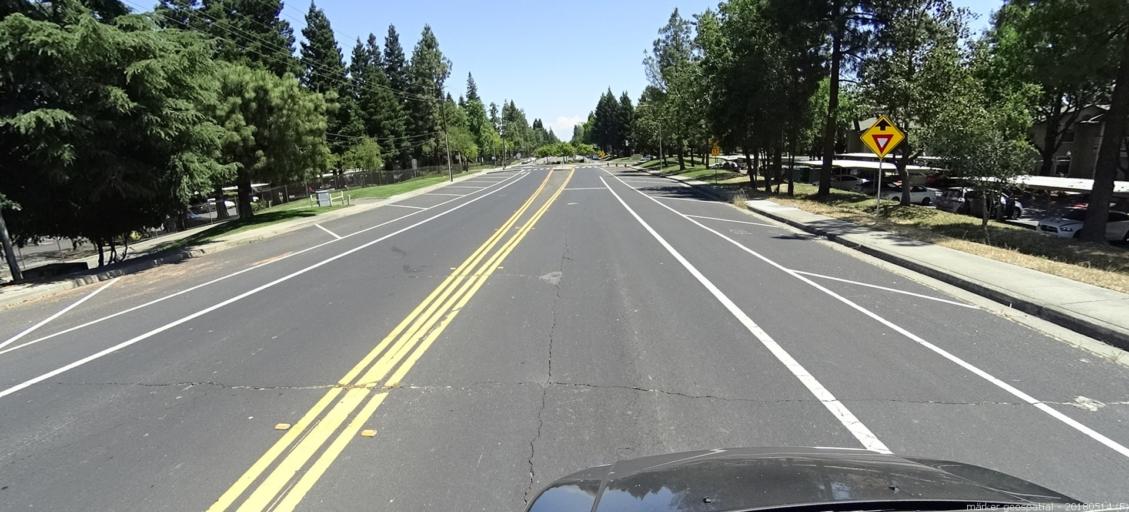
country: US
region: California
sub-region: Sacramento County
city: Sacramento
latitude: 38.6274
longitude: -121.5101
